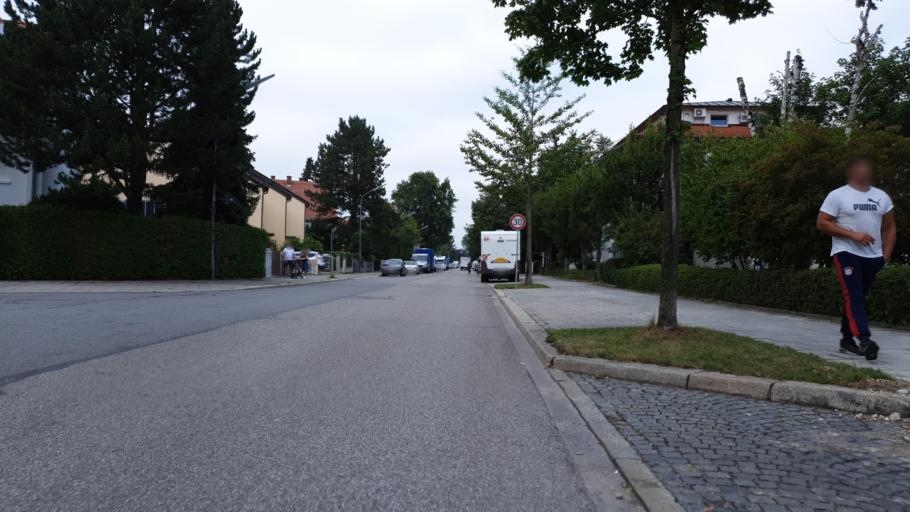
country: DE
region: Bavaria
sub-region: Upper Bavaria
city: Pasing
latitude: 48.1544
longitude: 11.4774
